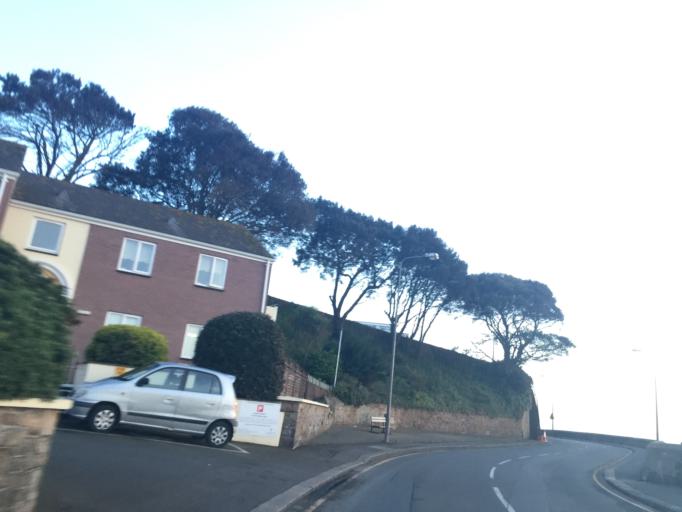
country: JE
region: St Helier
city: Saint Helier
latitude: 49.1785
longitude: -2.1087
